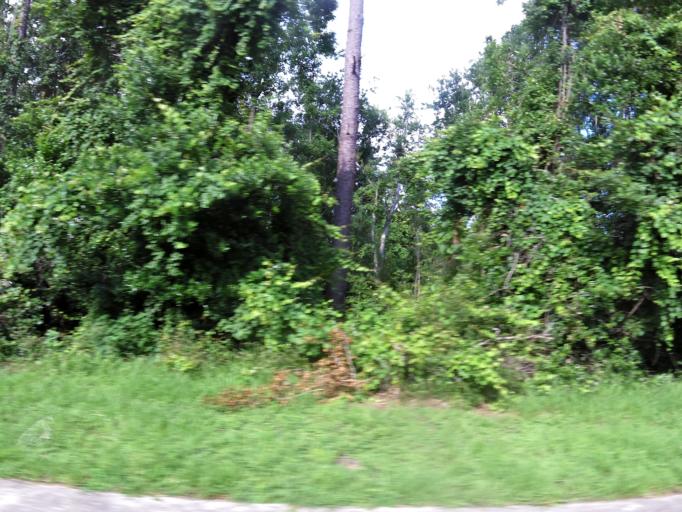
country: US
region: Florida
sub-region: Clay County
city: Green Cove Springs
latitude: 29.9928
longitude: -81.6988
